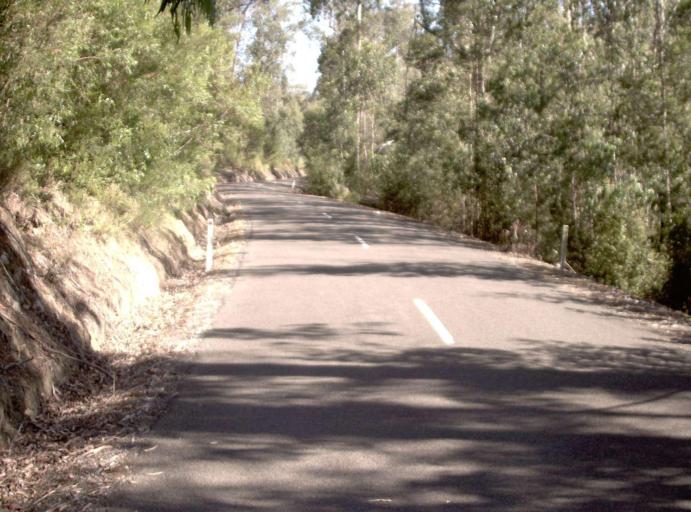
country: AU
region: Victoria
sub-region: East Gippsland
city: Lakes Entrance
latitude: -37.5140
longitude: 148.5484
